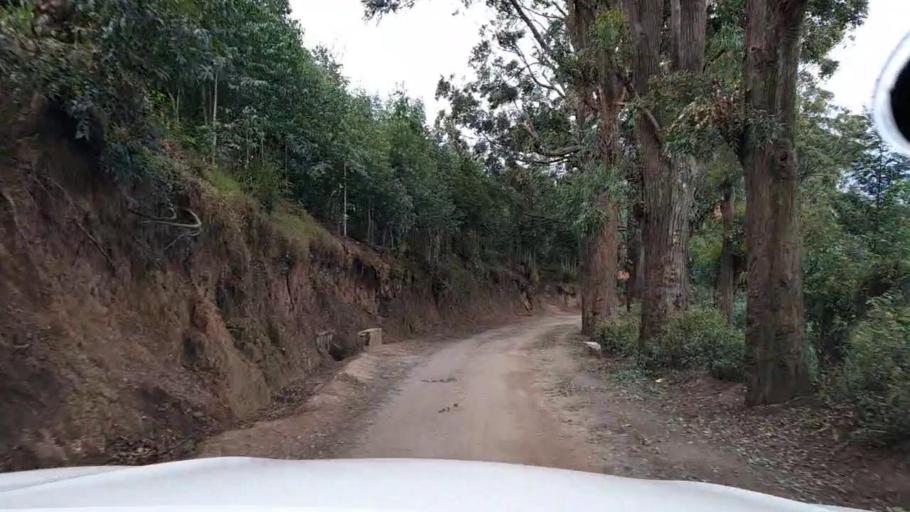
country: BI
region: Kayanza
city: Kayanza
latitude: -2.7956
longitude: 29.5092
